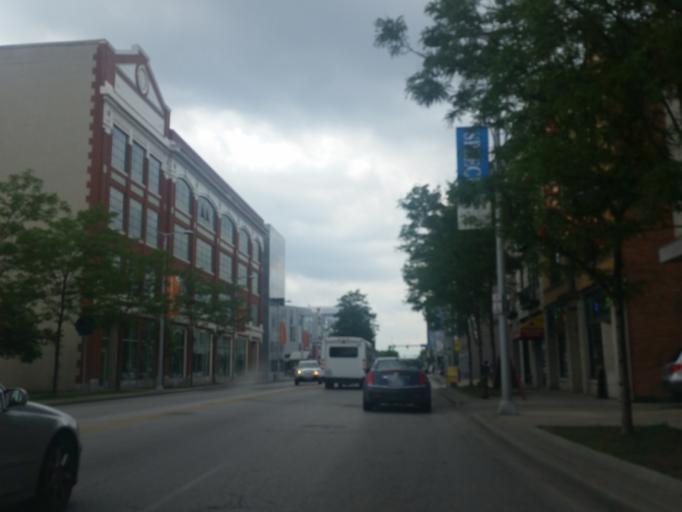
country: US
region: Ohio
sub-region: Cuyahoga County
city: East Cleveland
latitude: 41.5113
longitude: -81.6025
